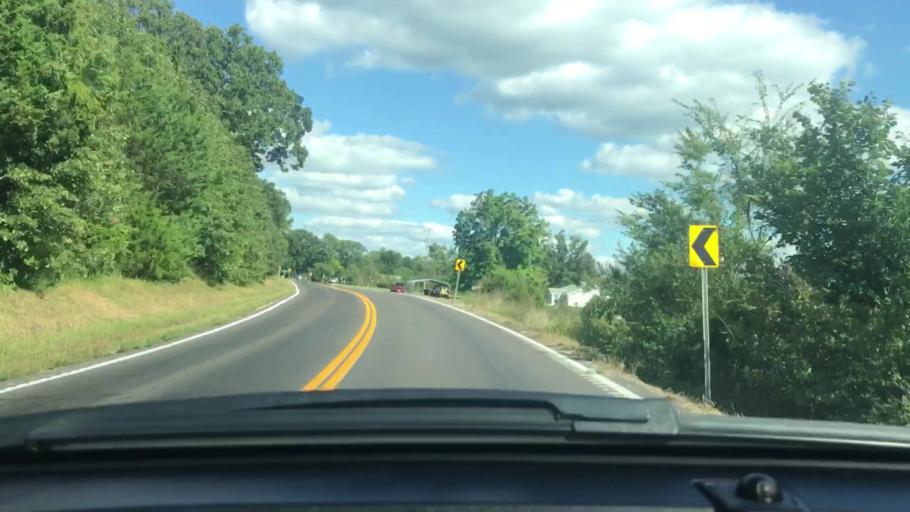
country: US
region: Missouri
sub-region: Wright County
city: Mountain Grove
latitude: 37.2544
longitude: -92.3054
